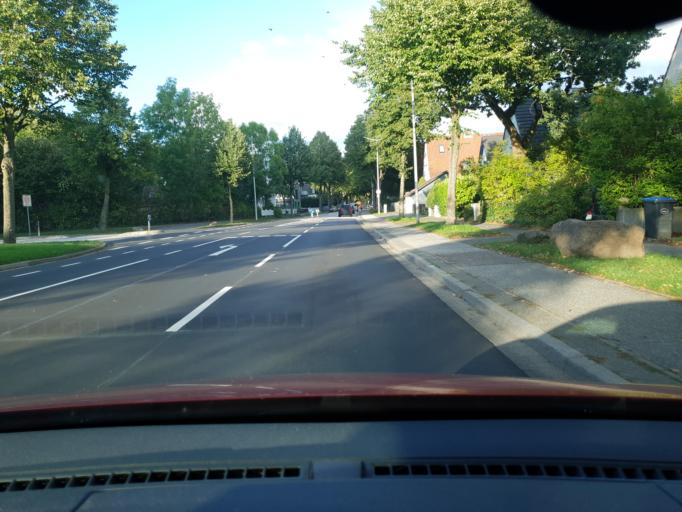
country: DE
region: Schleswig-Holstein
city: Kronshagen
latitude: 54.3421
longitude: 10.0933
